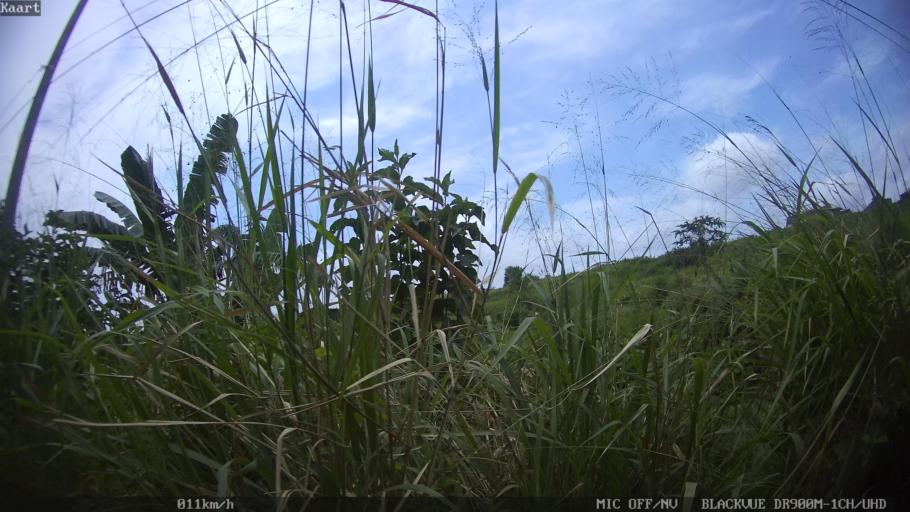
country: ID
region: Lampung
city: Bandarlampung
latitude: -5.4080
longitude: 105.1985
